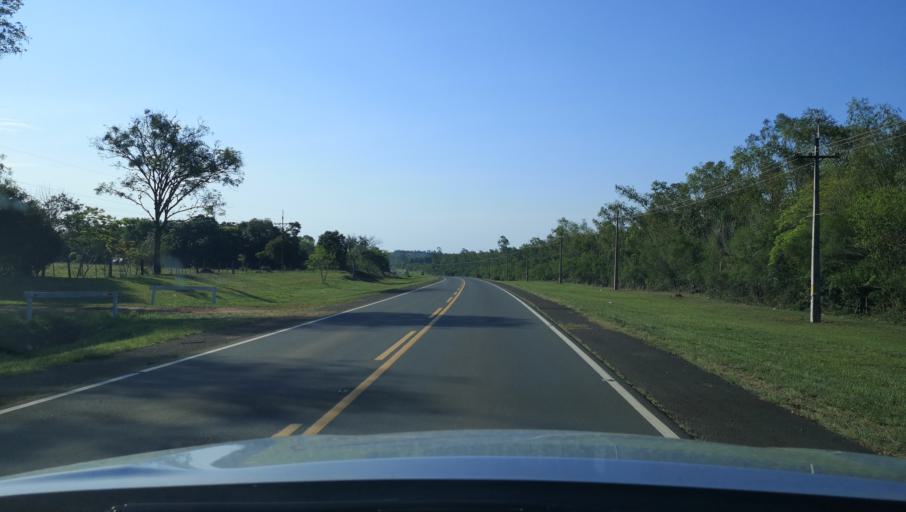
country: PY
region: Misiones
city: Santa Maria
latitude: -26.7601
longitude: -57.0341
